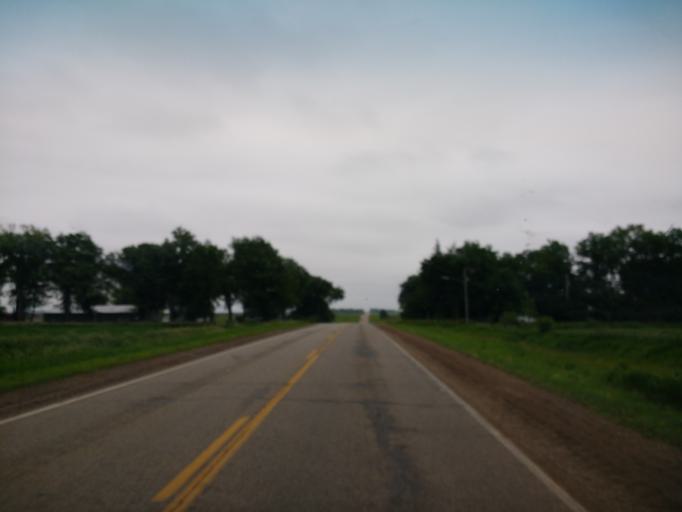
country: US
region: Iowa
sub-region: Dickinson County
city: Milford
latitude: 43.3280
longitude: -95.1135
